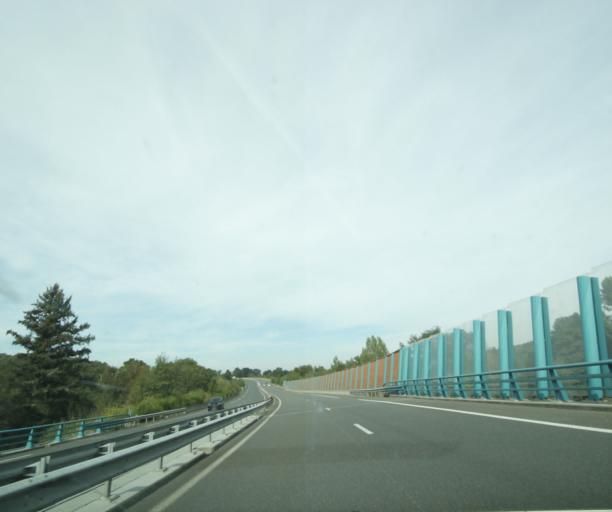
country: FR
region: Auvergne
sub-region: Departement de l'Allier
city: Lapalisse
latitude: 46.2312
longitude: 3.6481
